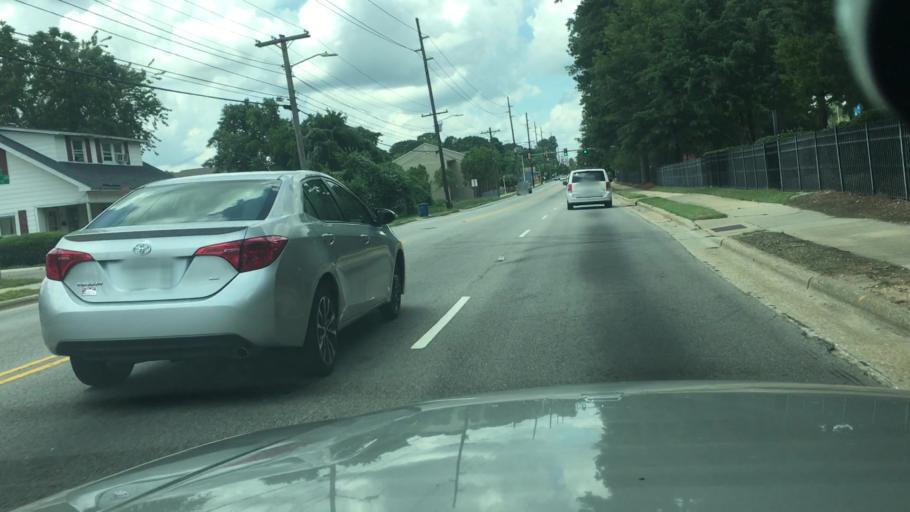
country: US
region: North Carolina
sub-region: Cumberland County
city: Fayetteville
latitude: 35.0731
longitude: -78.8956
